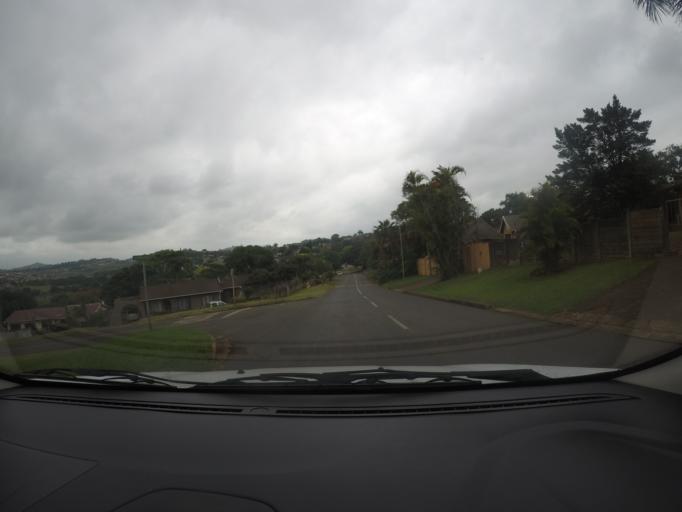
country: ZA
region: KwaZulu-Natal
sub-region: uThungulu District Municipality
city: Empangeni
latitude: -28.7656
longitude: 31.8880
